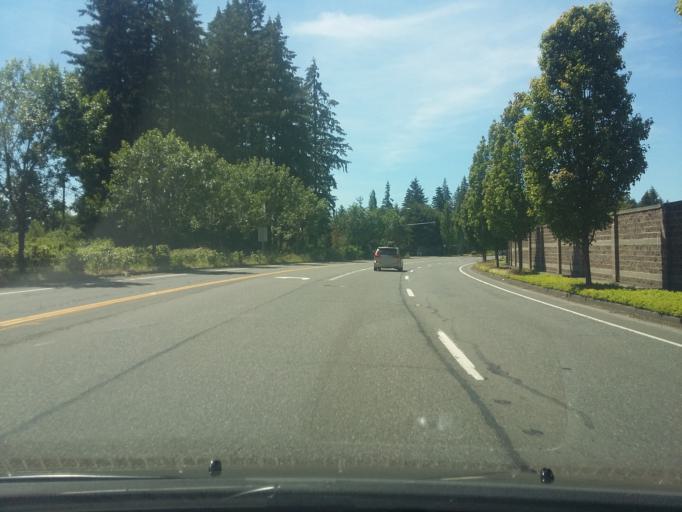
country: US
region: Washington
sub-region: Clark County
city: Mill Plain
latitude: 45.6831
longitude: -122.5099
